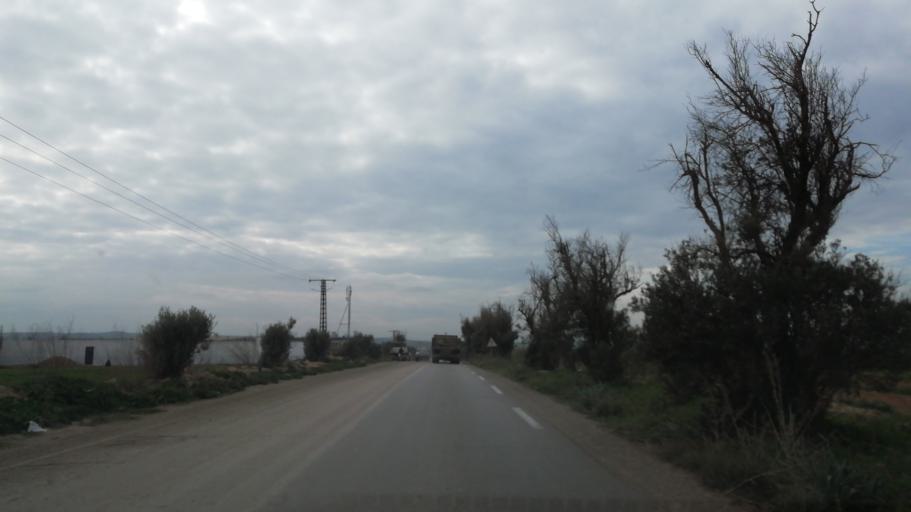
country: DZ
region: Oran
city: Ain el Bya
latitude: 35.7851
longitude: -0.3437
